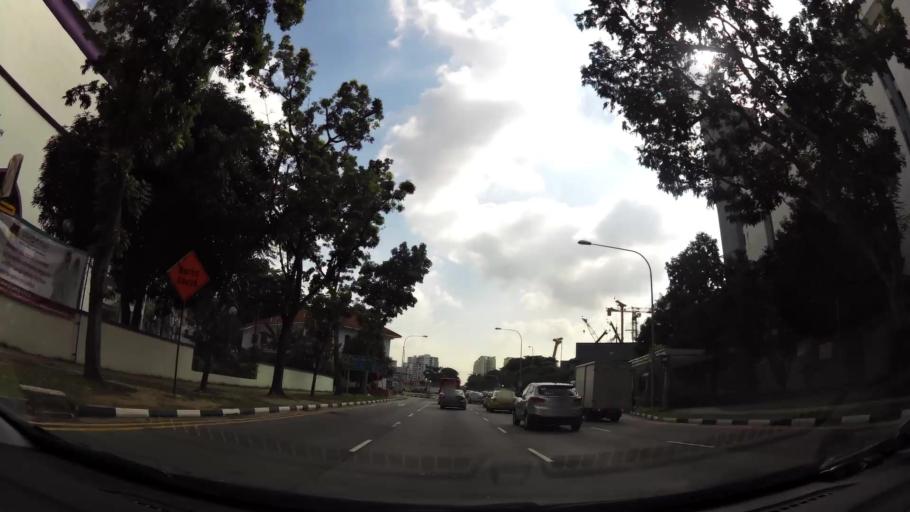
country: SG
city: Singapore
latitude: 1.3168
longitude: 103.8914
